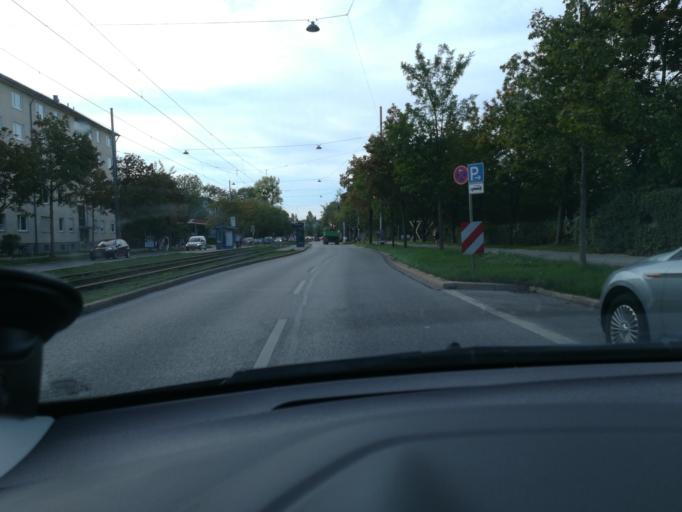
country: DE
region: Bavaria
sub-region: Upper Bavaria
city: Pasing
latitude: 48.1519
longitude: 11.5160
